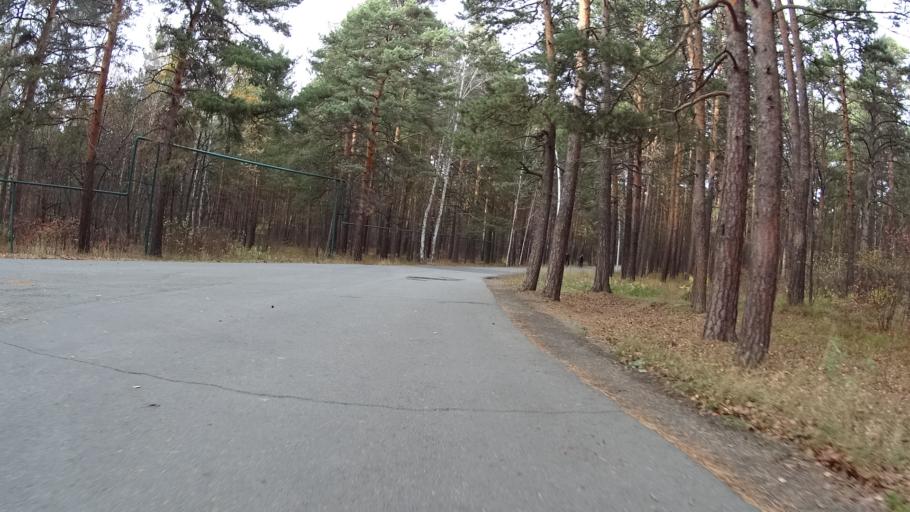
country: RU
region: Chelyabinsk
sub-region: Gorod Chelyabinsk
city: Chelyabinsk
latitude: 55.1403
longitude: 61.3491
